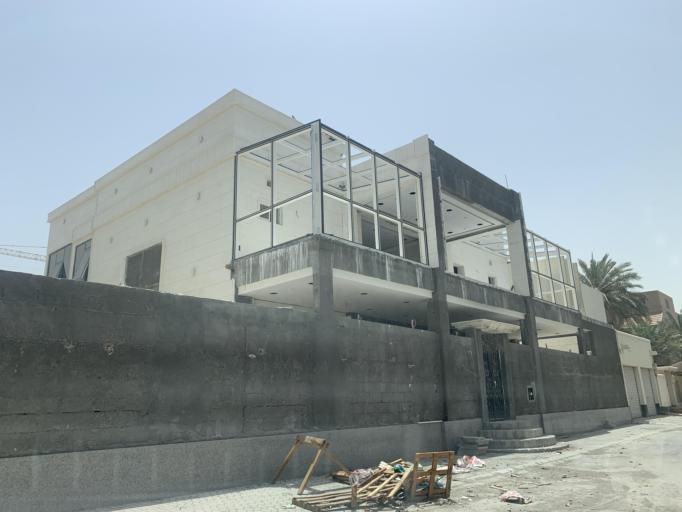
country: BH
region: Northern
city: Madinat `Isa
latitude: 26.1582
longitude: 50.5255
